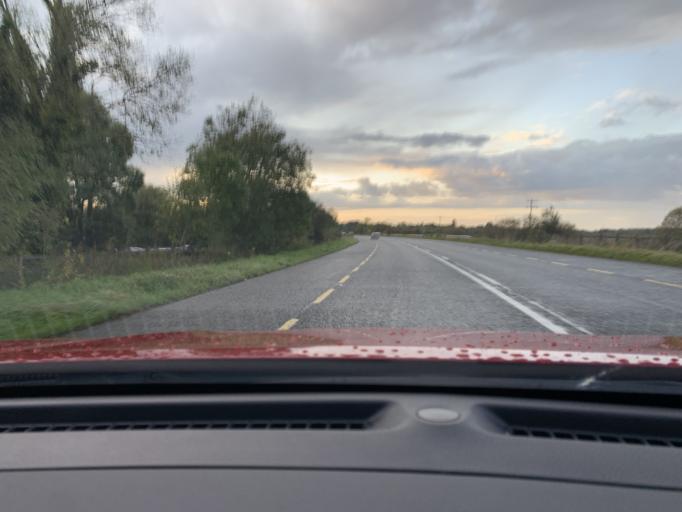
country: IE
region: Connaught
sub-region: County Leitrim
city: Carrick-on-Shannon
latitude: 53.9481
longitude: -8.1246
